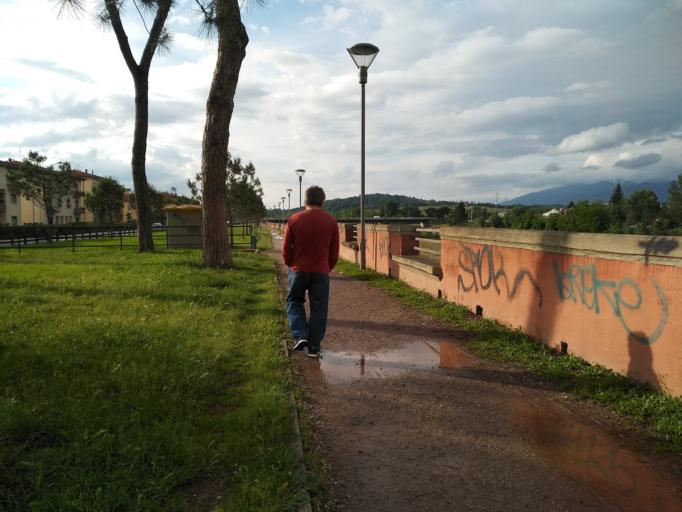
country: IT
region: Tuscany
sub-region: Province of Arezzo
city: San Giovanni Valdarno
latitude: 43.5684
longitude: 11.5331
